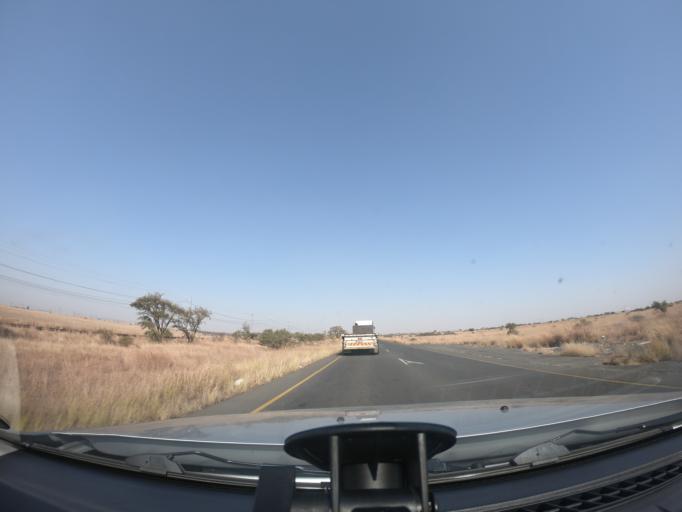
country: ZA
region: KwaZulu-Natal
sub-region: uThukela District Municipality
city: Ladysmith
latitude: -28.7581
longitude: 29.8211
